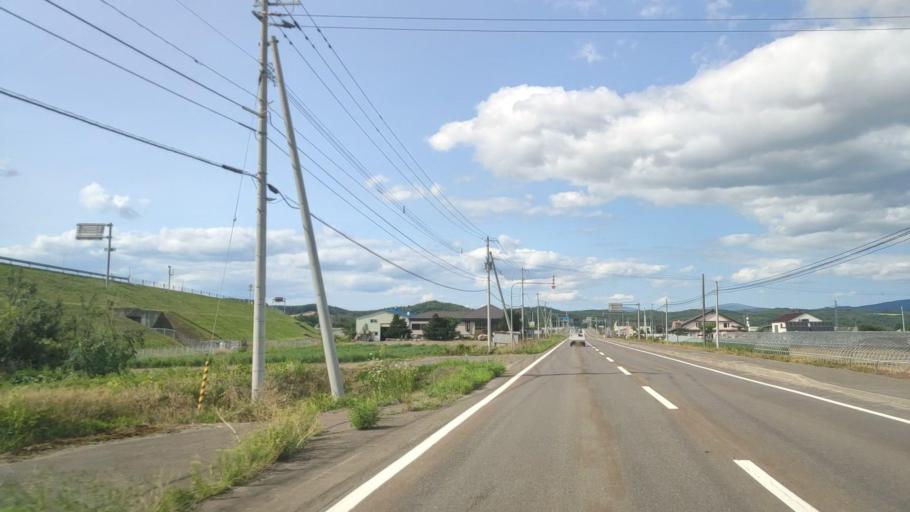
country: JP
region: Hokkaido
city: Nayoro
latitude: 44.3676
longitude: 142.4361
